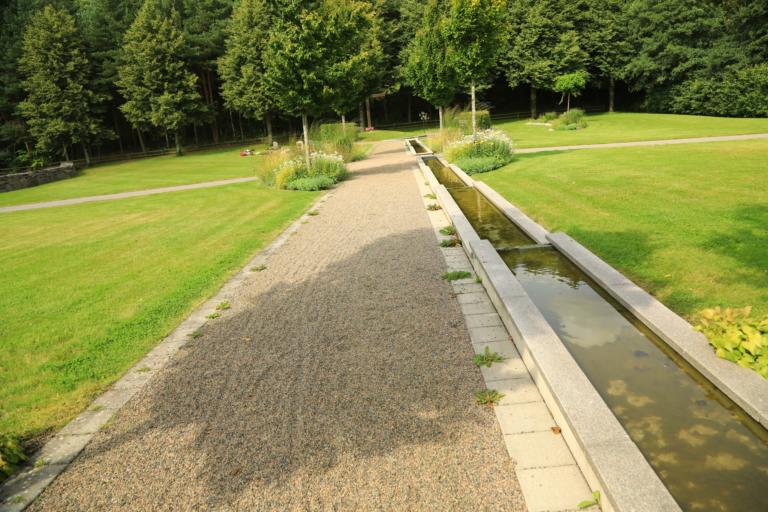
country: SE
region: Halland
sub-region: Varbergs Kommun
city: Veddige
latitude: 57.1893
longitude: 12.2784
